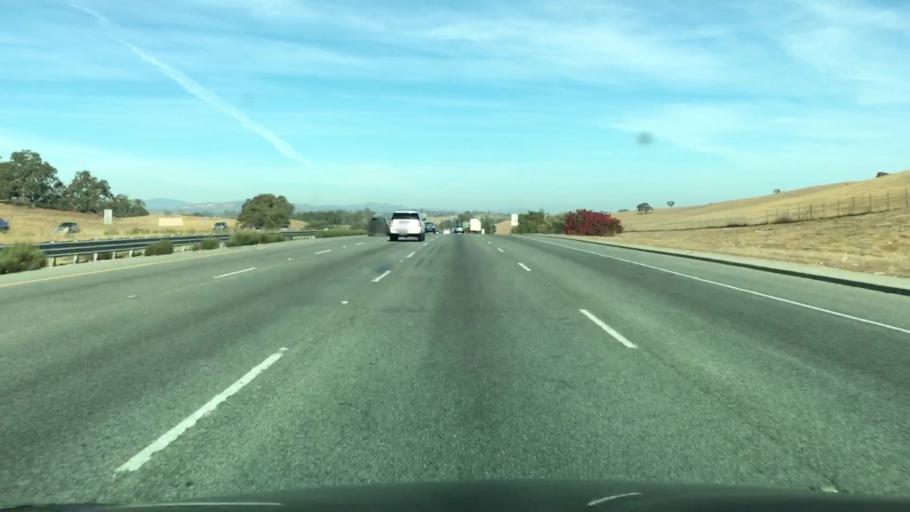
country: US
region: California
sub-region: San Mateo County
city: Ladera
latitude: 37.3953
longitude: -122.1811
